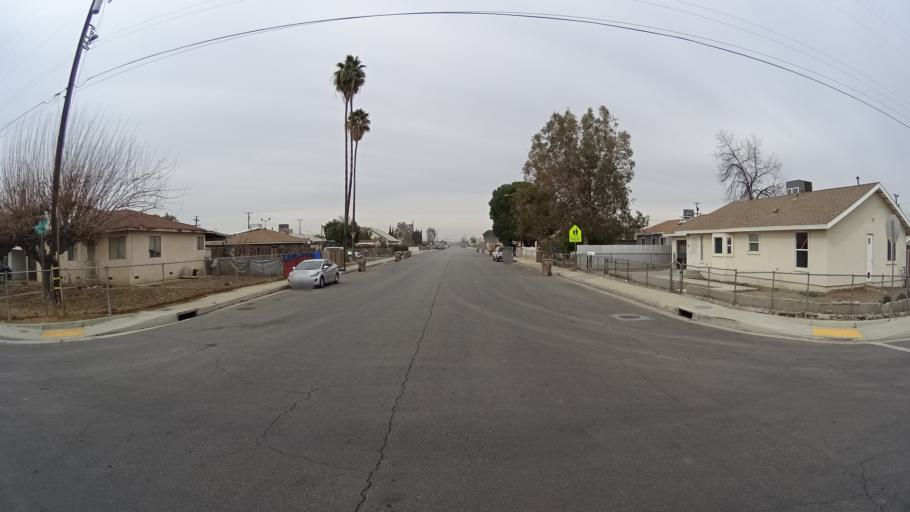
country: US
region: California
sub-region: Kern County
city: Bakersfield
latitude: 35.3695
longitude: -118.9906
